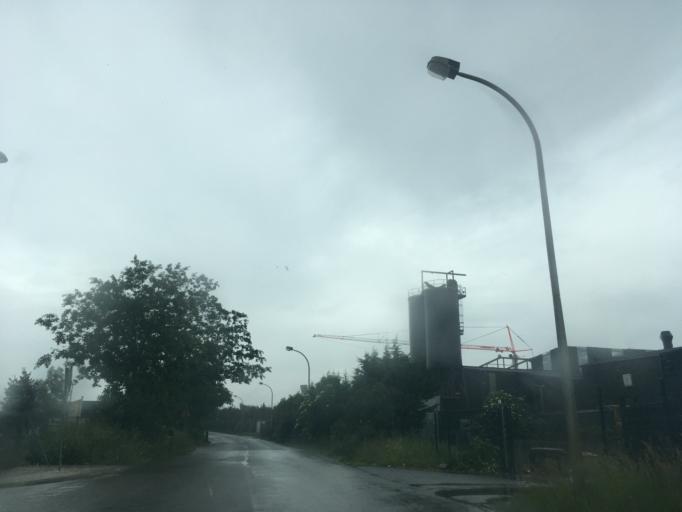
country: FR
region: Poitou-Charentes
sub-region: Departement de la Charente
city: Saint-Brice
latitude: 45.6781
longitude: -0.3042
